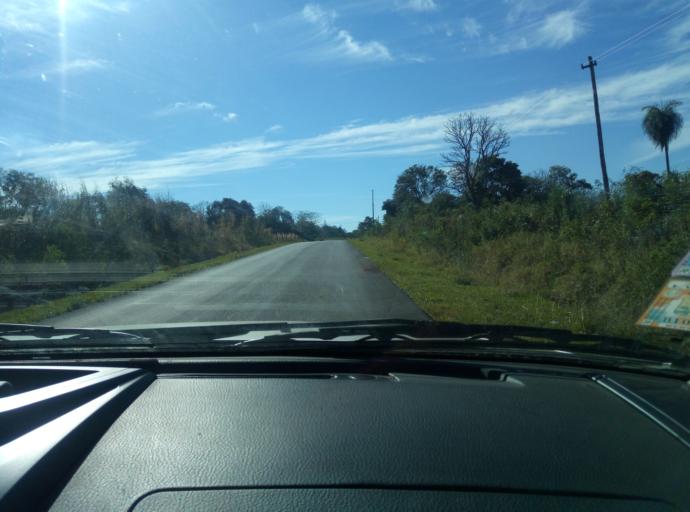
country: PY
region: Caaguazu
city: Carayao
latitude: -25.1695
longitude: -56.3130
